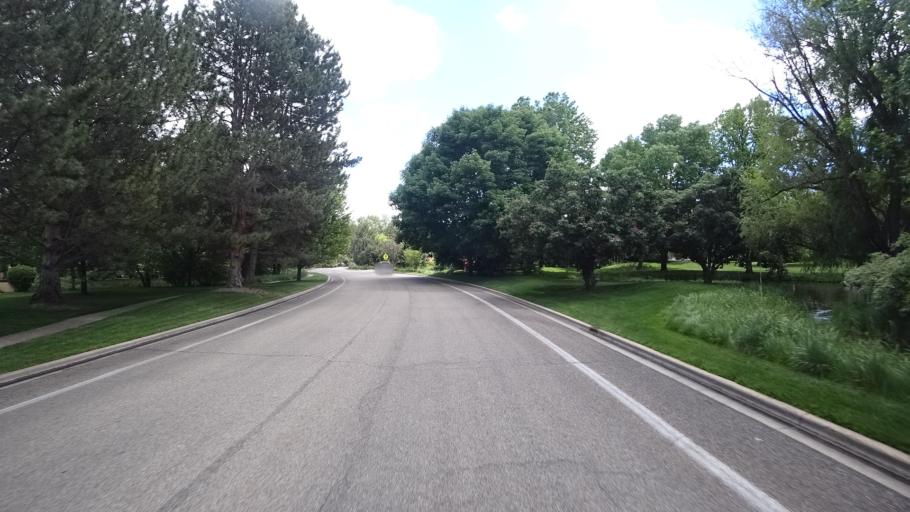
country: US
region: Idaho
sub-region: Ada County
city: Boise
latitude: 43.5874
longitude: -116.1676
